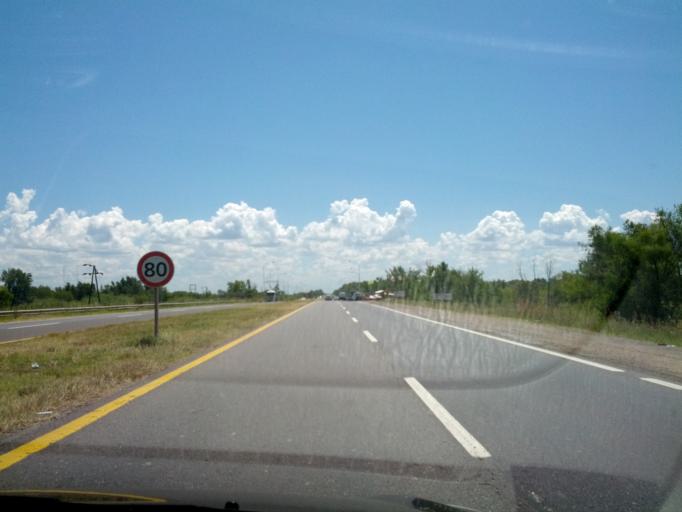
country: AR
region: Entre Rios
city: Villa Paranacito
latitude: -33.7312
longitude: -58.8534
